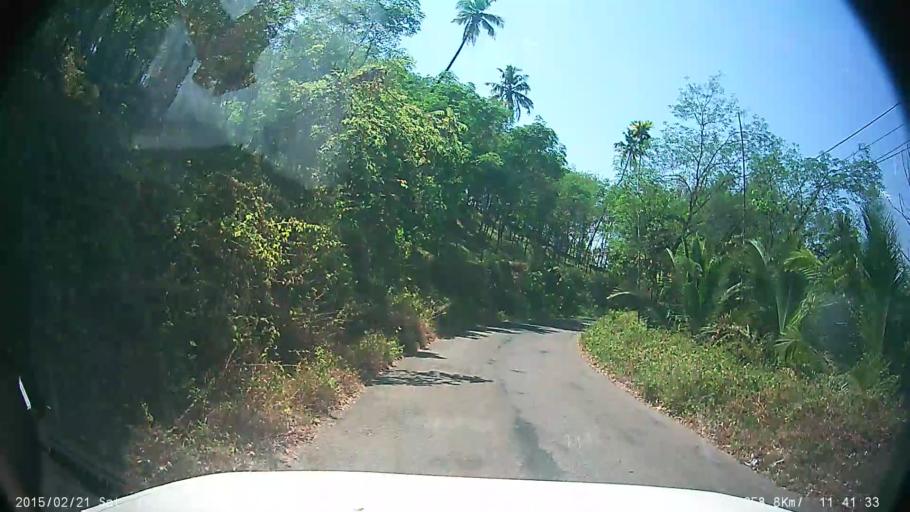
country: IN
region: Kerala
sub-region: Kottayam
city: Lalam
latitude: 9.7941
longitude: 76.7283
